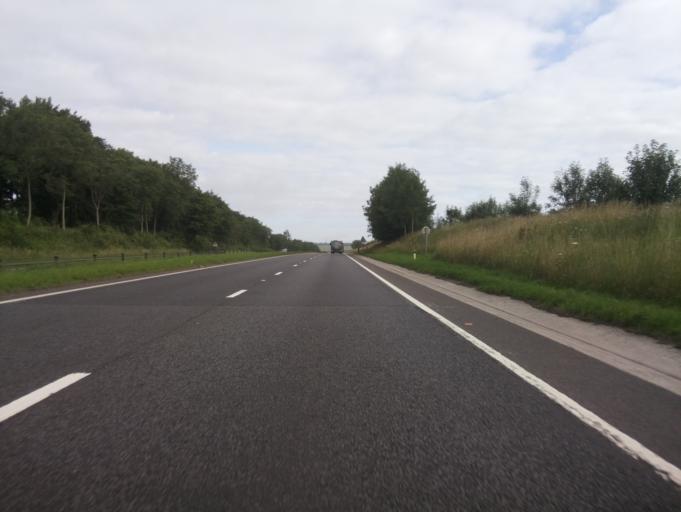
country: GB
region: England
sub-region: Gloucestershire
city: Charlton Kings
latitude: 51.8044
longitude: -2.0587
